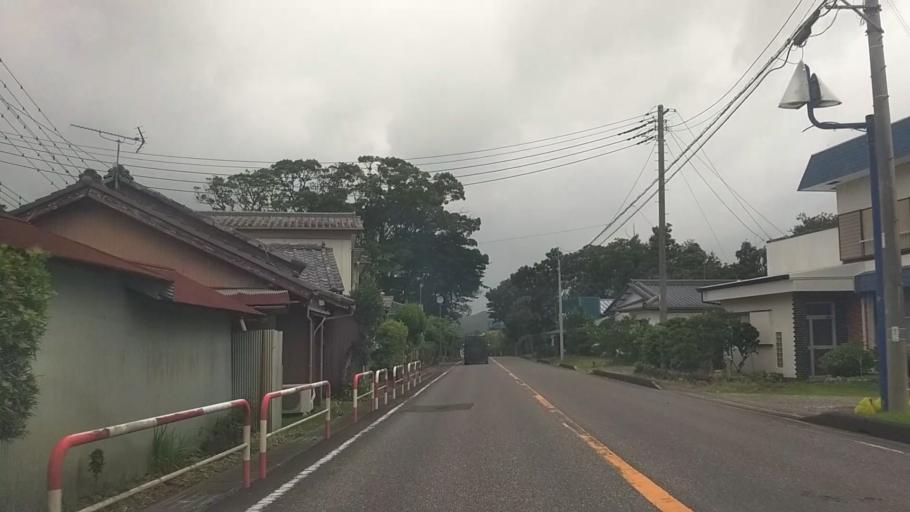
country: JP
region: Chiba
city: Kawaguchi
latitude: 35.1317
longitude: 140.0137
